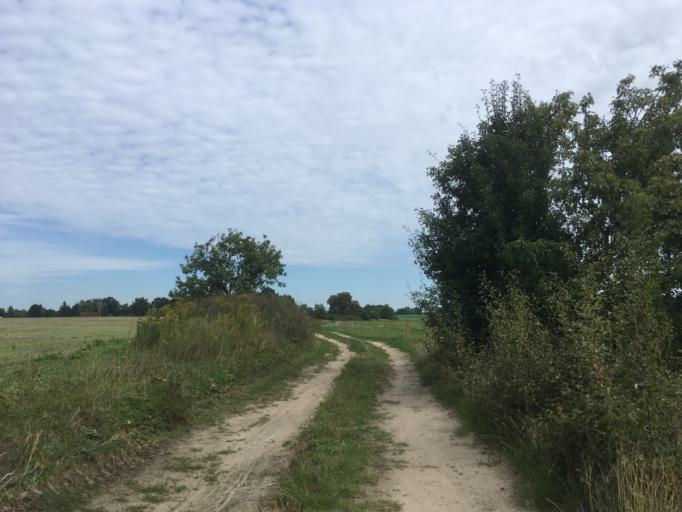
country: DE
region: Brandenburg
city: Wandlitz
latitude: 52.7588
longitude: 13.4152
